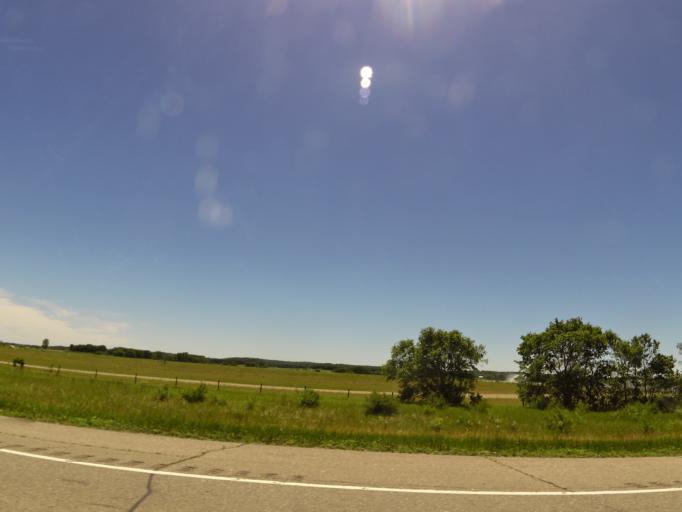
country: US
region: Minnesota
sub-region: Otter Tail County
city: Perham
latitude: 46.5789
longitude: -95.5633
